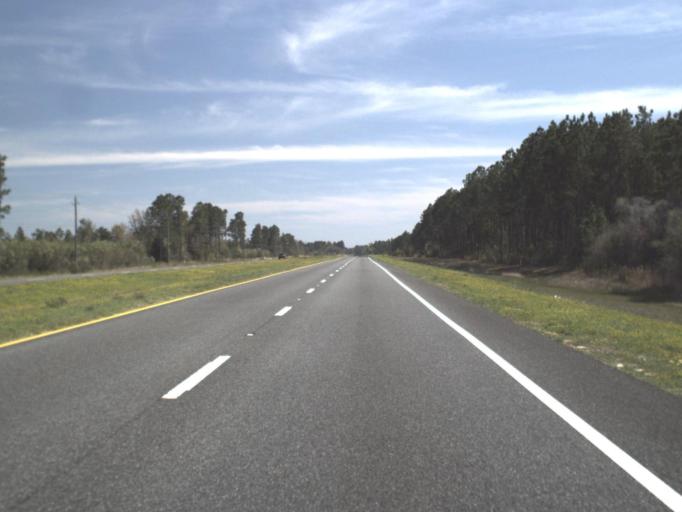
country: US
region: Florida
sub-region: Bay County
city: Lynn Haven
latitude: 30.3108
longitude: -85.6530
